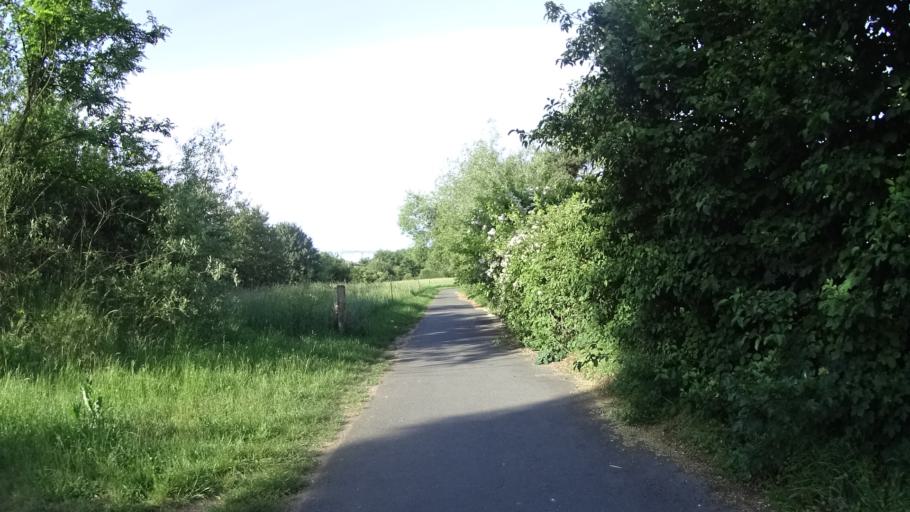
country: DE
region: Bavaria
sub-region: Regierungsbezirk Unterfranken
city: Kahl am Main
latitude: 50.0640
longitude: 8.9910
